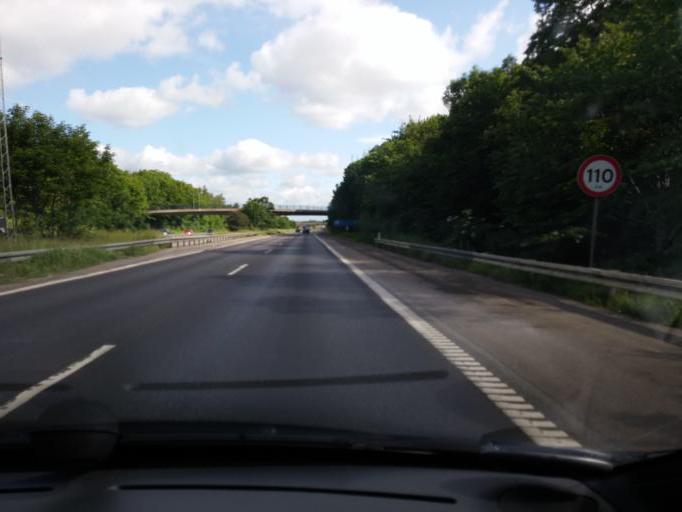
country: DK
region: Capital Region
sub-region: Fureso Kommune
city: Farum
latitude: 55.8086
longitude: 12.3818
